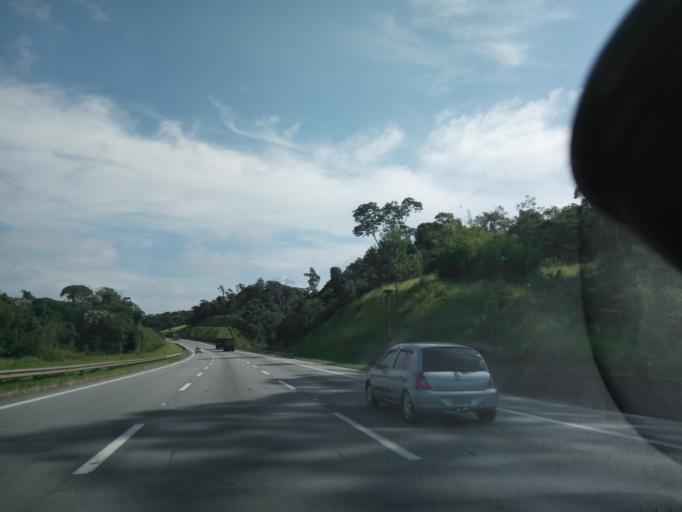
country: BR
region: Sao Paulo
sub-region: Embu
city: Embu
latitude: -23.6679
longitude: -46.8239
